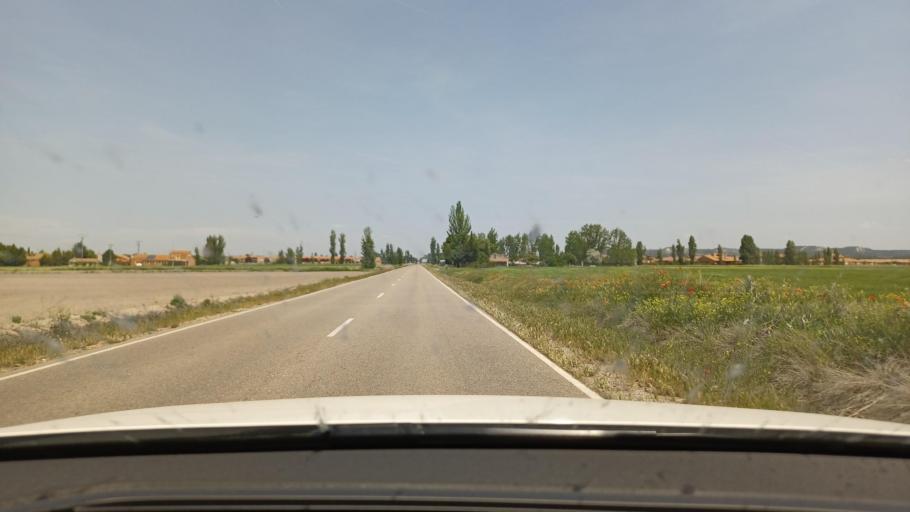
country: ES
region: Castille and Leon
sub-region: Provincia de Valladolid
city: Aldeamayor de San Martin
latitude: 41.5202
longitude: -4.6329
